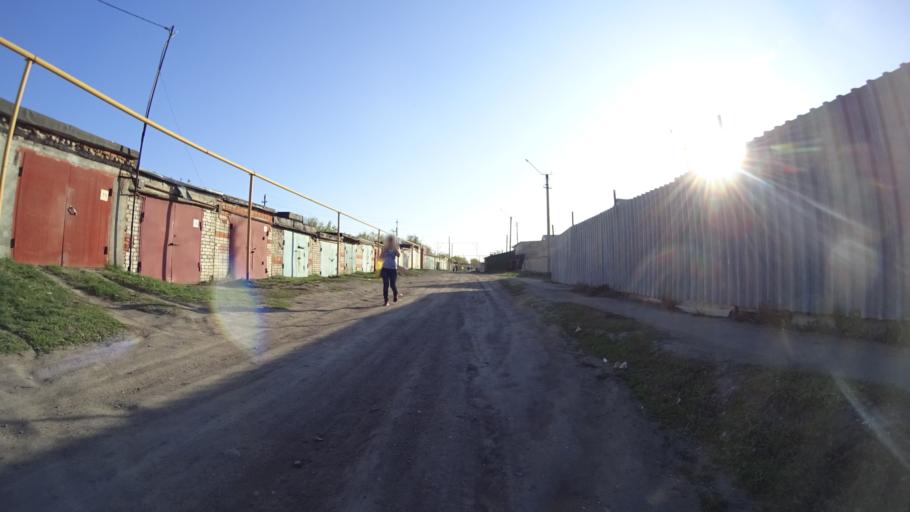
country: RU
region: Chelyabinsk
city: Troitsk
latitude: 54.0861
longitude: 61.5330
